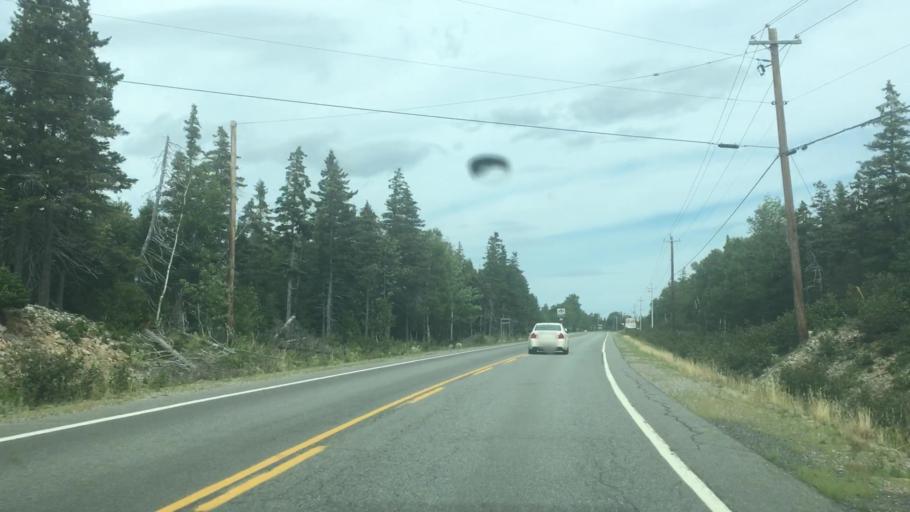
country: CA
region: Nova Scotia
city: Sydney Mines
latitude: 46.5143
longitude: -60.4289
